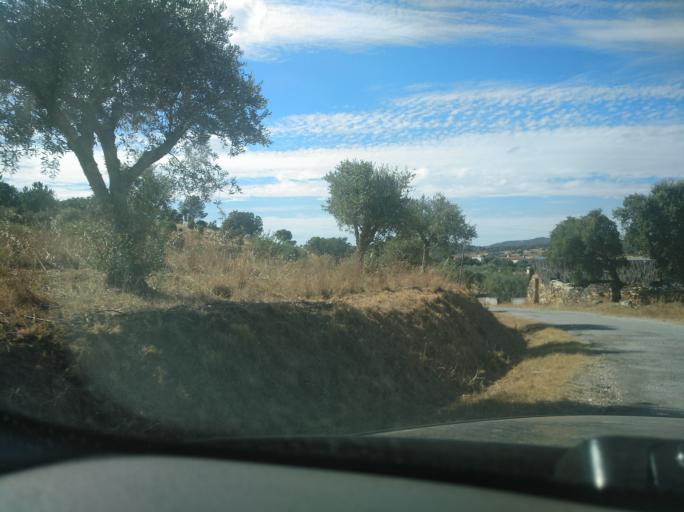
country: ES
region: Extremadura
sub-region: Provincia de Badajoz
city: La Codosera
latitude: 39.1525
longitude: -7.1648
